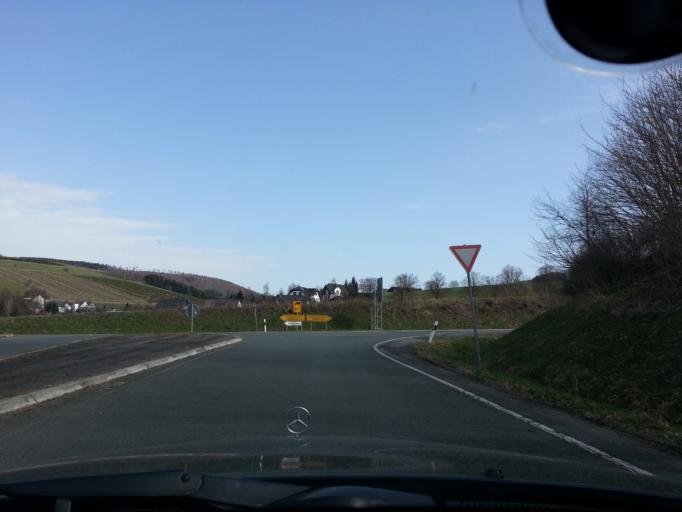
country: DE
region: North Rhine-Westphalia
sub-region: Regierungsbezirk Arnsberg
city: Bad Fredeburg
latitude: 51.2541
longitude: 8.3682
